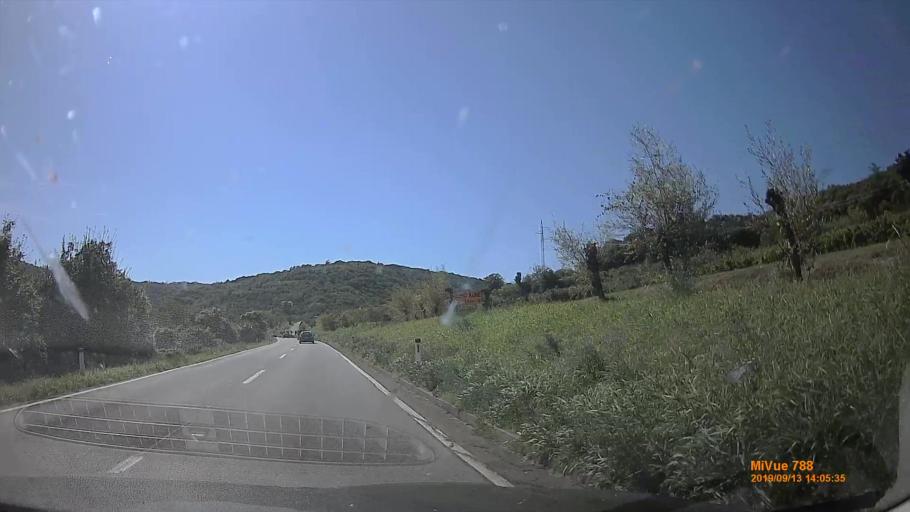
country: SI
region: Koper-Capodistria
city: Koper
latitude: 45.5227
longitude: 13.7285
